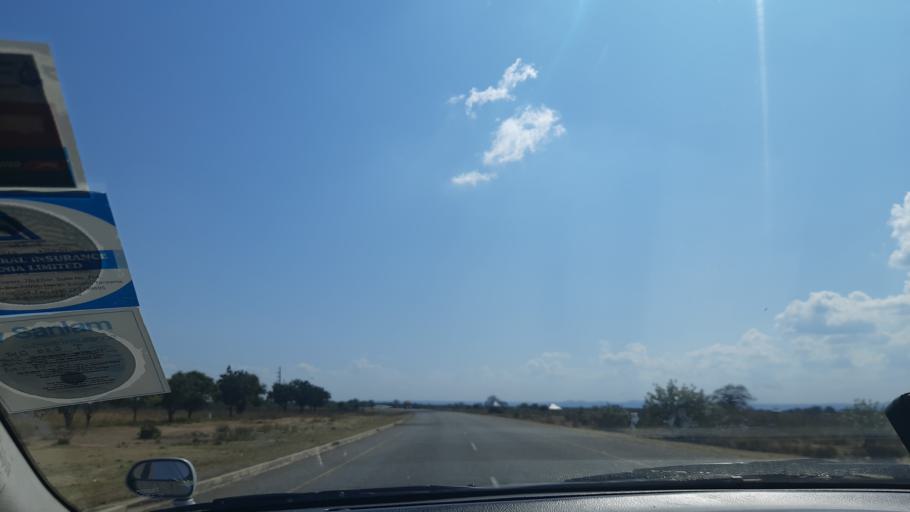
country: TZ
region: Singida
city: Kintinku
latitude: -5.8809
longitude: 35.1376
